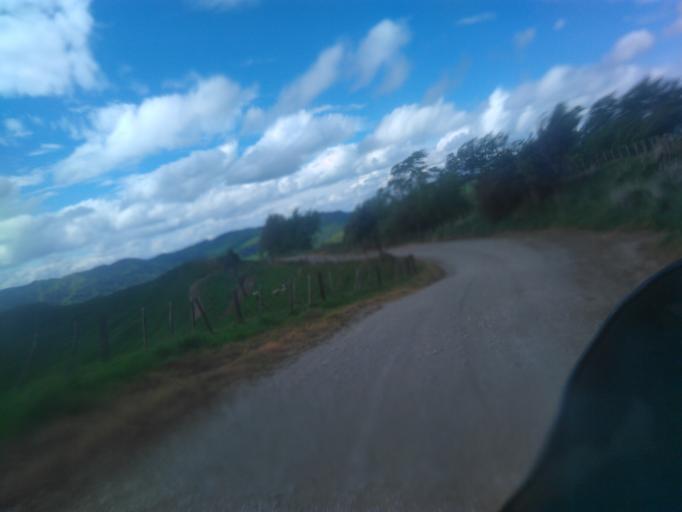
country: NZ
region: Hawke's Bay
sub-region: Wairoa District
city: Wairoa
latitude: -38.7678
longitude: 177.6399
